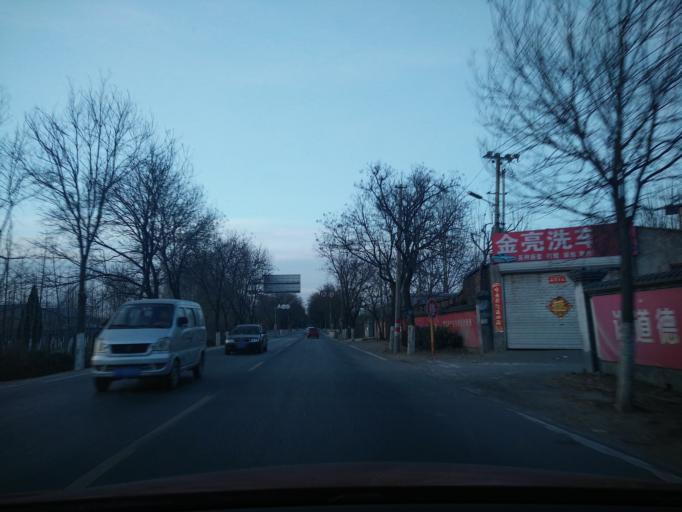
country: CN
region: Beijing
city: Qingyundian
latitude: 39.6806
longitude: 116.4970
